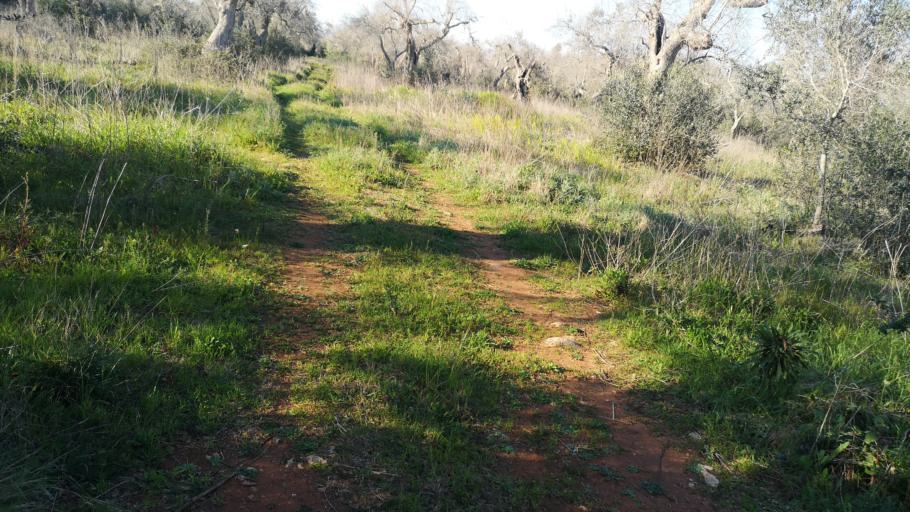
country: IT
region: Apulia
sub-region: Provincia di Lecce
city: Surano
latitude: 40.0069
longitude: 18.3394
